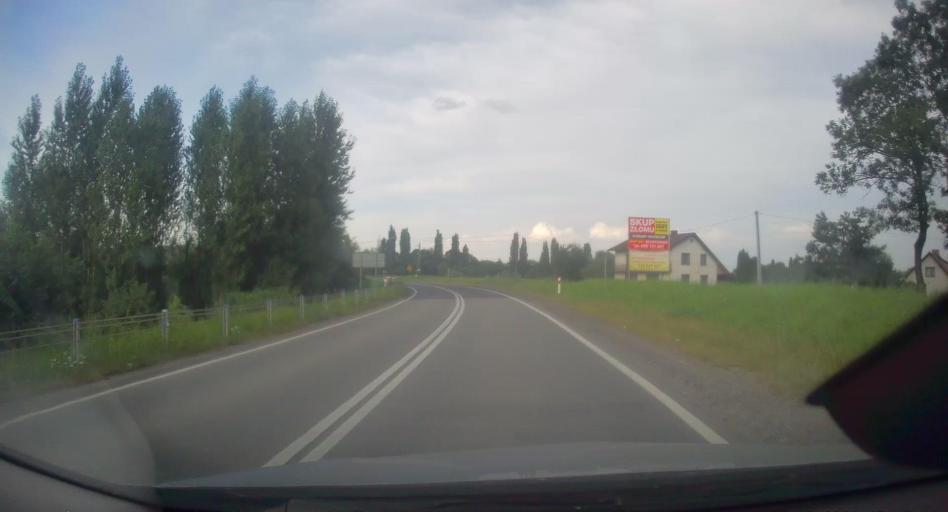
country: PL
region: Lesser Poland Voivodeship
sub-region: Powiat brzeski
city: Szczurowa
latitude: 50.1626
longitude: 20.5712
